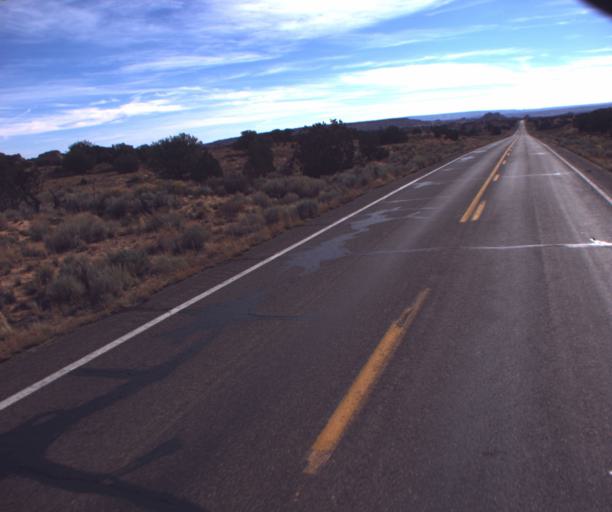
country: US
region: Arizona
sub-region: Coconino County
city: Kaibito
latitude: 36.6517
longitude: -111.2372
